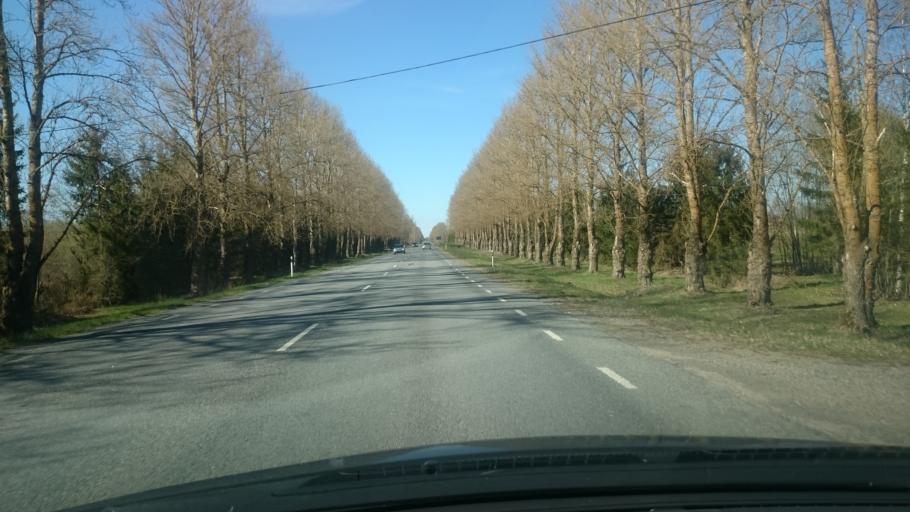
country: EE
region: Polvamaa
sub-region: Polva linn
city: Polva
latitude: 58.2741
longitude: 27.0026
